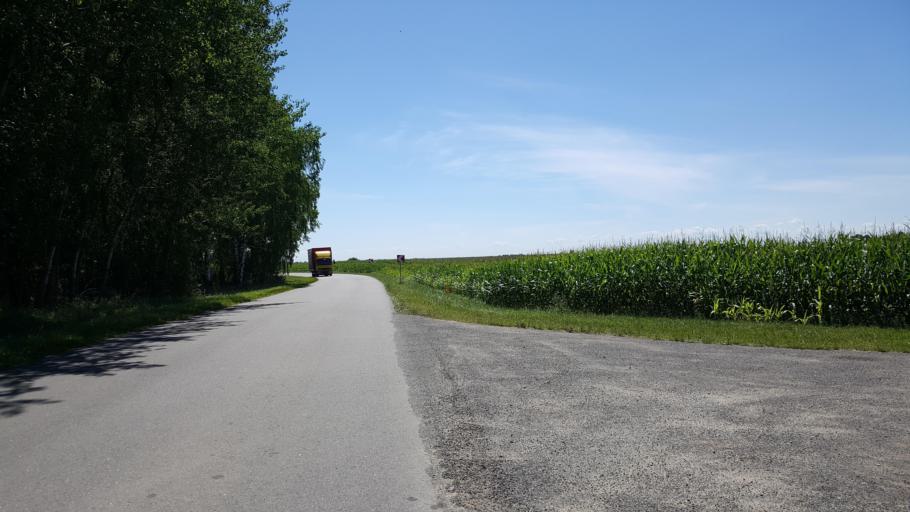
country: BY
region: Brest
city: Charnawchytsy
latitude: 52.2249
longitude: 23.8049
